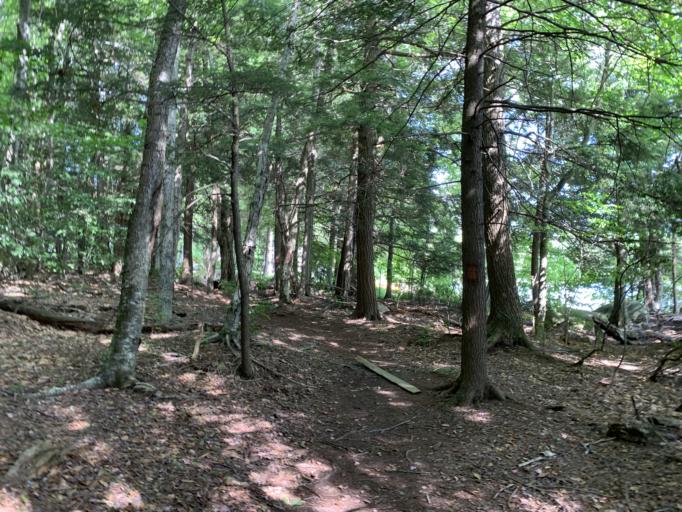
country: US
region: Massachusetts
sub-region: Berkshire County
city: Becket
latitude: 42.2955
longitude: -73.0645
